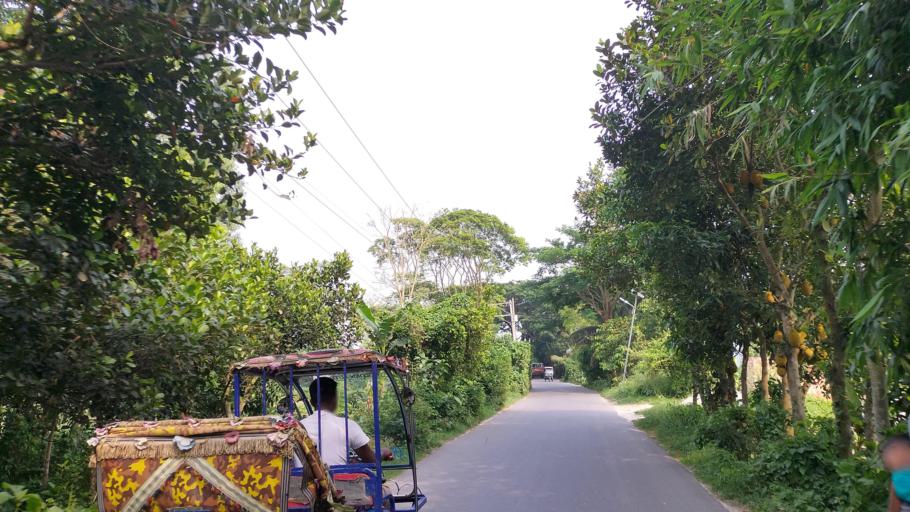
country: BD
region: Dhaka
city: Azimpur
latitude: 23.6774
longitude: 90.3165
